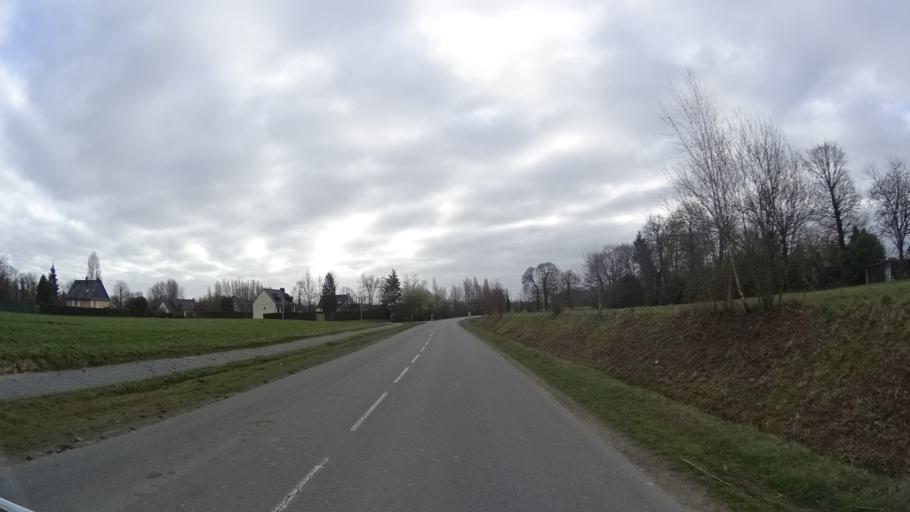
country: FR
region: Brittany
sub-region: Departement d'Ille-et-Vilaine
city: Saint-Gilles
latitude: 48.1824
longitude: -1.8529
